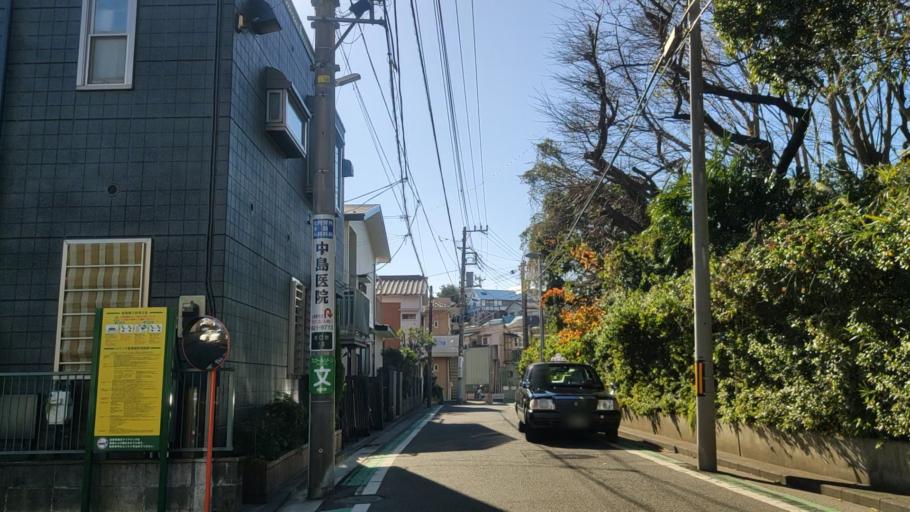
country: JP
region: Kanagawa
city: Yokohama
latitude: 35.4257
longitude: 139.6465
